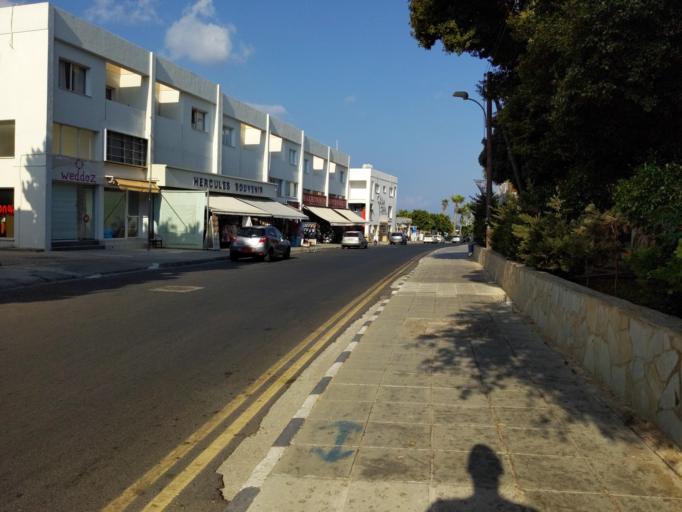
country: CY
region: Ammochostos
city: Protaras
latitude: 35.0281
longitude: 34.0429
